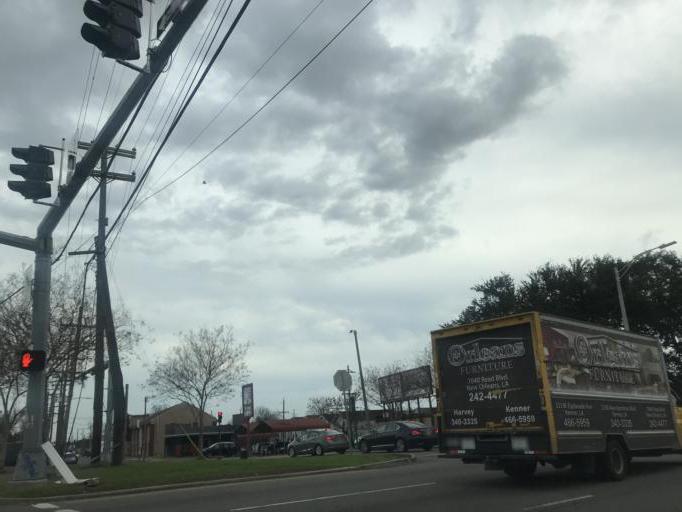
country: US
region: Louisiana
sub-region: Orleans Parish
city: New Orleans
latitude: 29.9464
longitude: -90.0888
